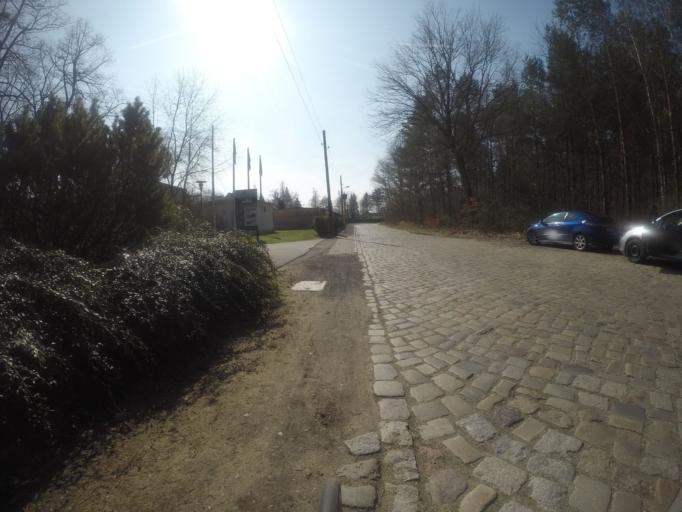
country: DE
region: Berlin
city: Schmockwitz
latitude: 52.3729
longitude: 13.6946
